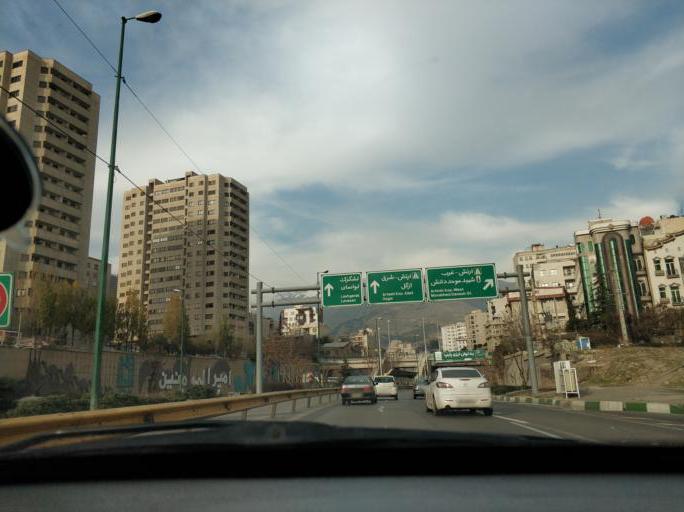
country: IR
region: Tehran
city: Tajrish
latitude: 35.7905
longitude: 51.4912
